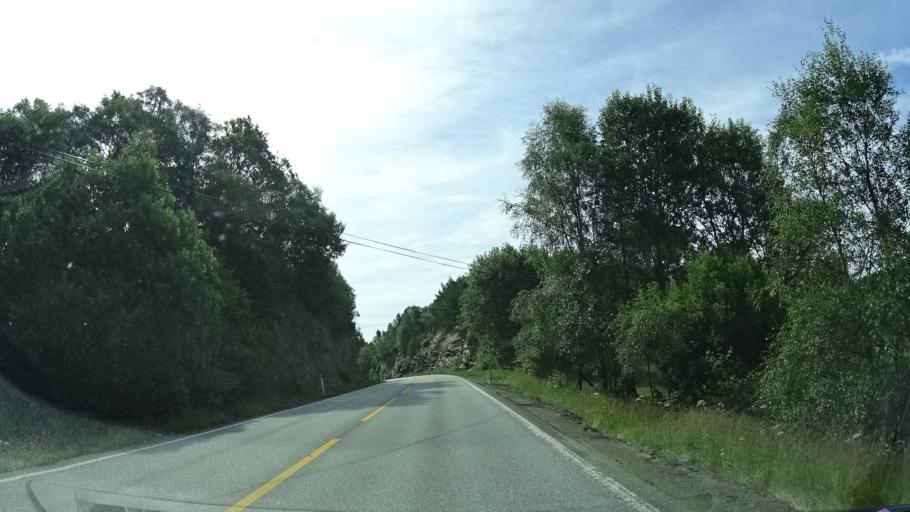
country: NO
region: Hordaland
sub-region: Bomlo
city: Mosterhamn
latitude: 59.6662
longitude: 5.4672
